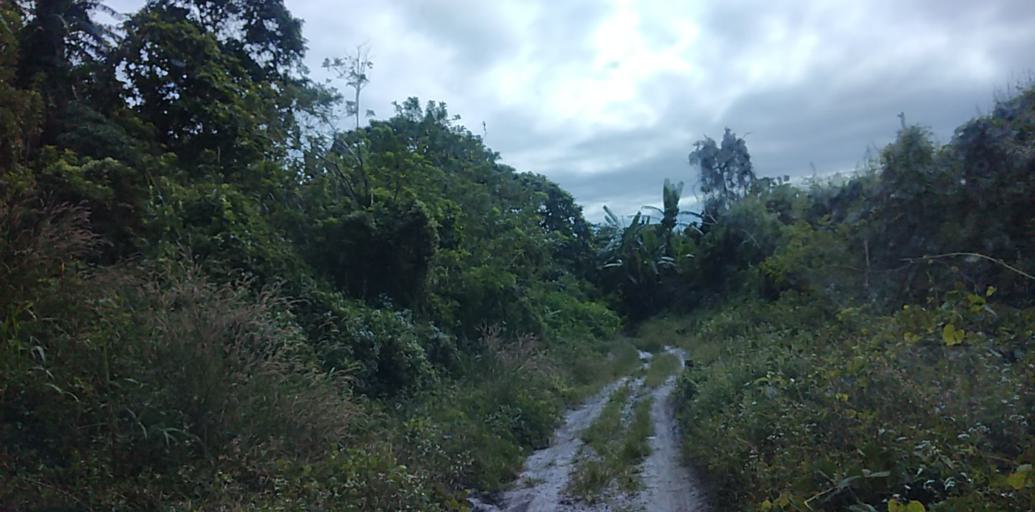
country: PH
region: Central Luzon
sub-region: Province of Pampanga
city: Babo-Pangulo
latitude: 15.1502
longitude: 120.4449
